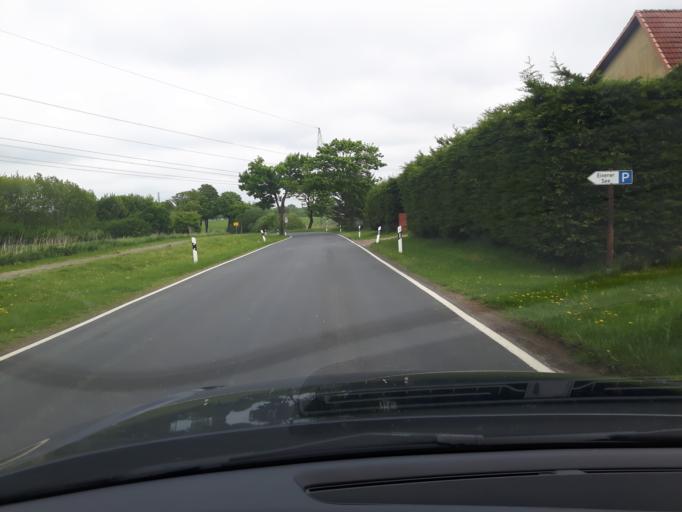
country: DE
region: Mecklenburg-Vorpommern
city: Tribsees
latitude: 54.1675
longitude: 12.7288
